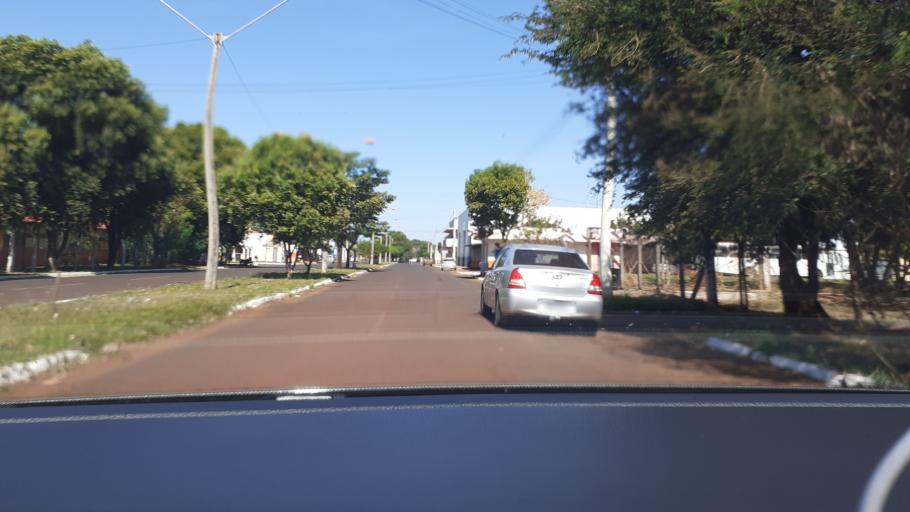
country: BR
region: Goias
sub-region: Itumbiara
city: Itumbiara
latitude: -18.4089
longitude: -49.2559
